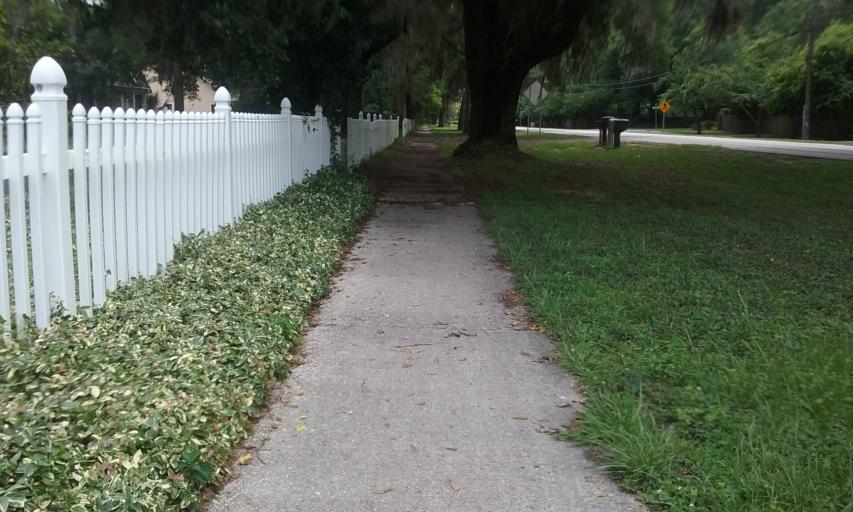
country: US
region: Florida
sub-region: Alachua County
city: Gainesville
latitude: 29.6814
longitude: -82.3596
